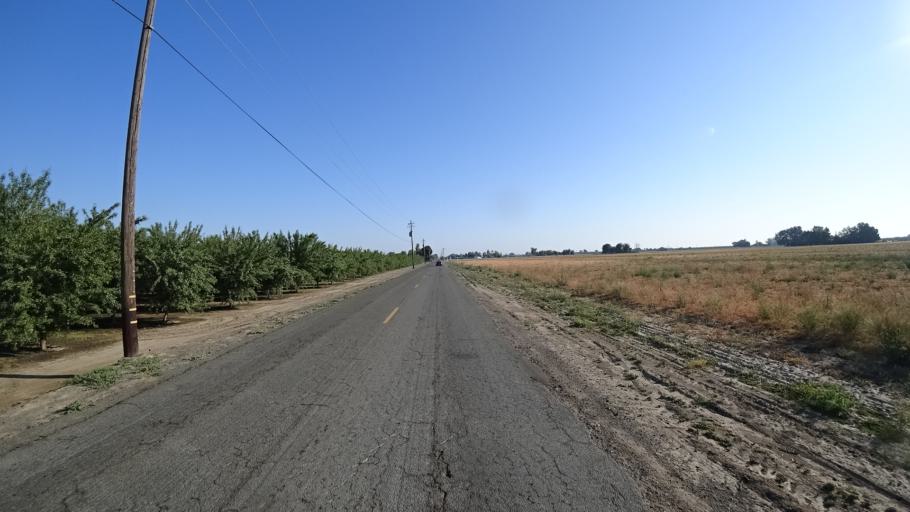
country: US
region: California
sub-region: Kings County
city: Lemoore
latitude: 36.2631
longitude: -119.7446
